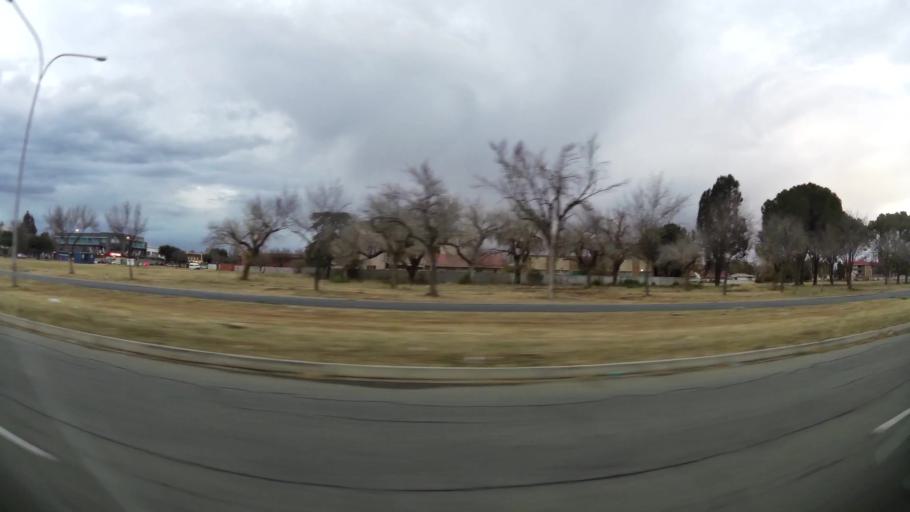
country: ZA
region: Orange Free State
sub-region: Lejweleputswa District Municipality
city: Welkom
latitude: -27.9651
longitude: 26.7443
